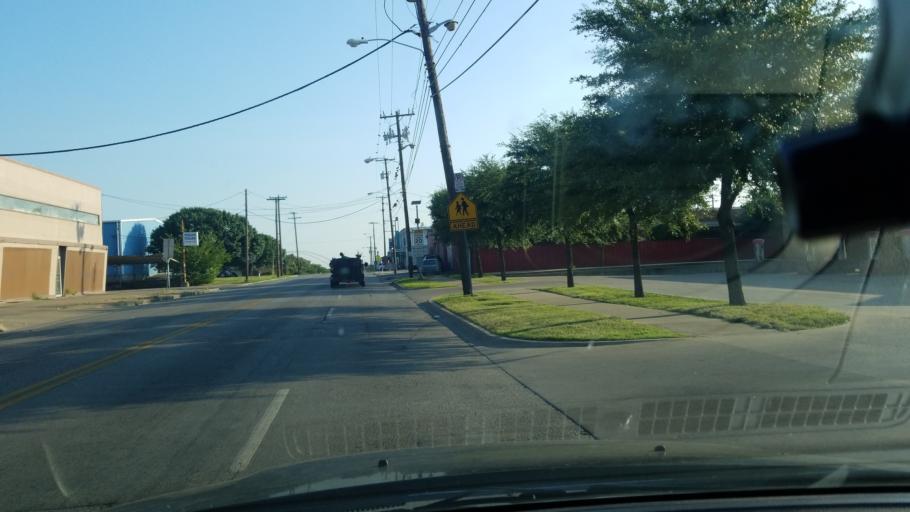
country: US
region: Texas
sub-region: Dallas County
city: Dallas
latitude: 32.7484
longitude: -96.8156
